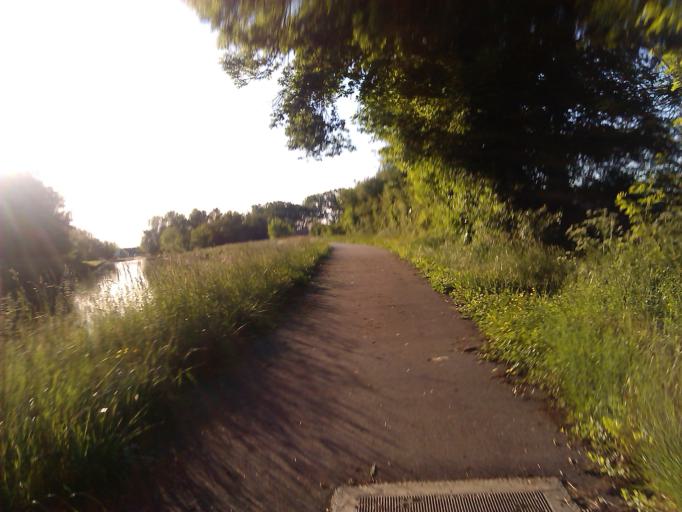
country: FR
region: Auvergne
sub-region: Departement de l'Allier
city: Dompierre-sur-Besbre
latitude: 46.5368
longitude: 3.7126
